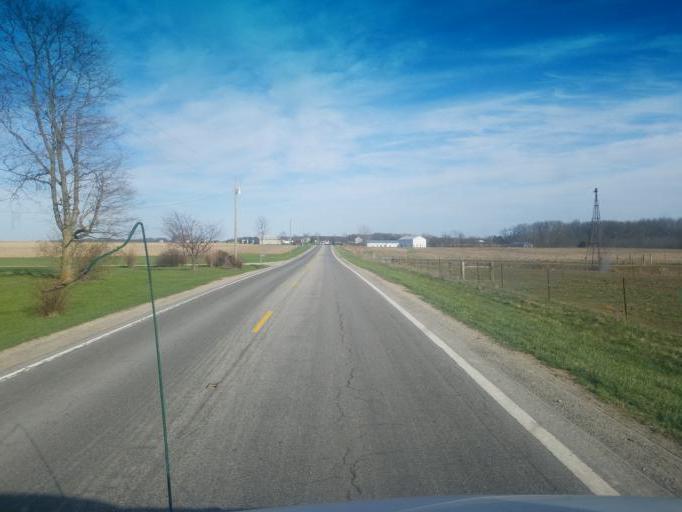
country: US
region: Ohio
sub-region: Shelby County
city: Jackson Center
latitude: 40.3399
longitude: -84.0272
